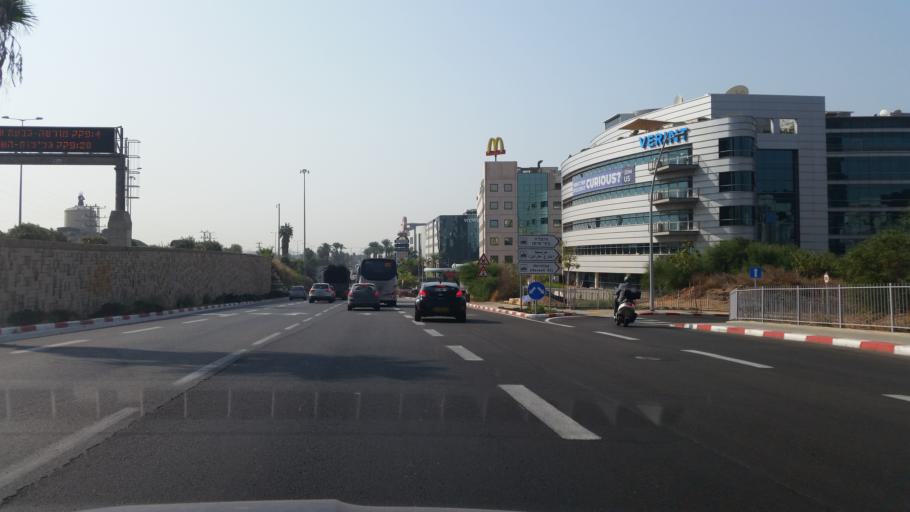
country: IL
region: Tel Aviv
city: Herzliyya
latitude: 32.1624
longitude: 34.8119
